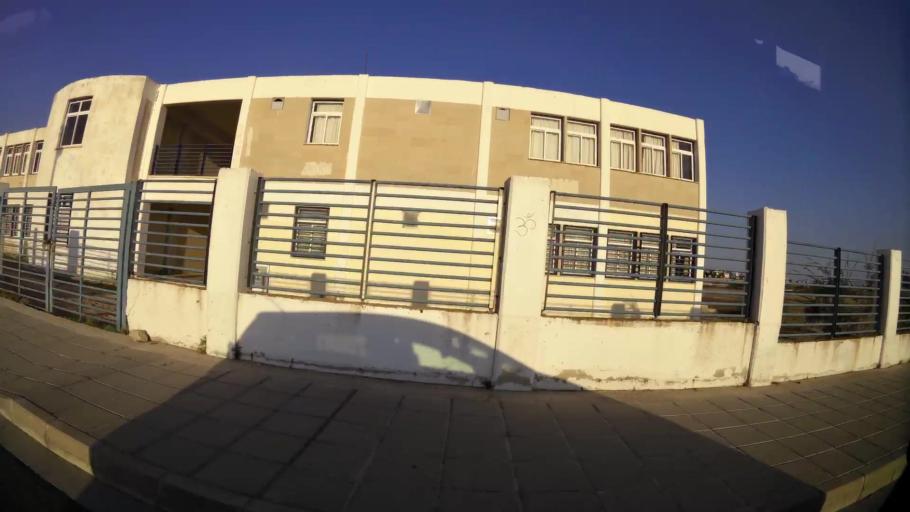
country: CY
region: Larnaka
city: Larnaca
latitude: 34.9196
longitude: 33.5934
